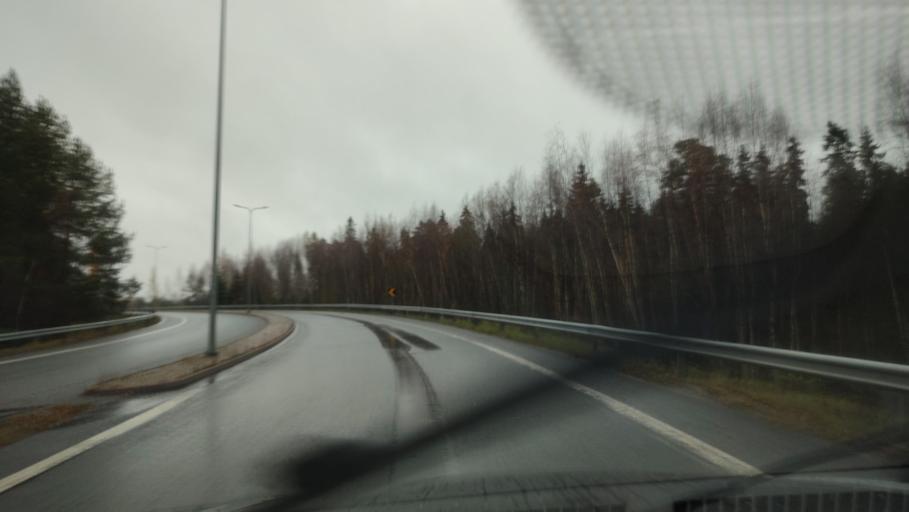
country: FI
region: Ostrobothnia
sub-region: Vaasa
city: Ristinummi
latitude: 63.0545
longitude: 21.7105
